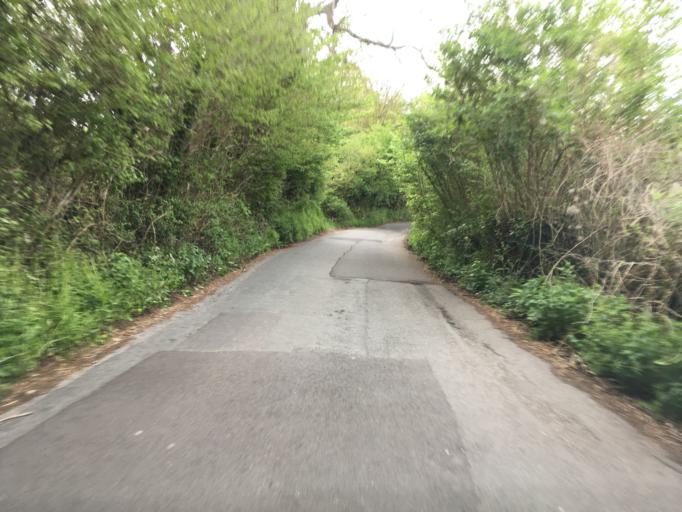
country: GB
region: England
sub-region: Bath and North East Somerset
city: Bath
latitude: 51.3557
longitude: -2.3387
